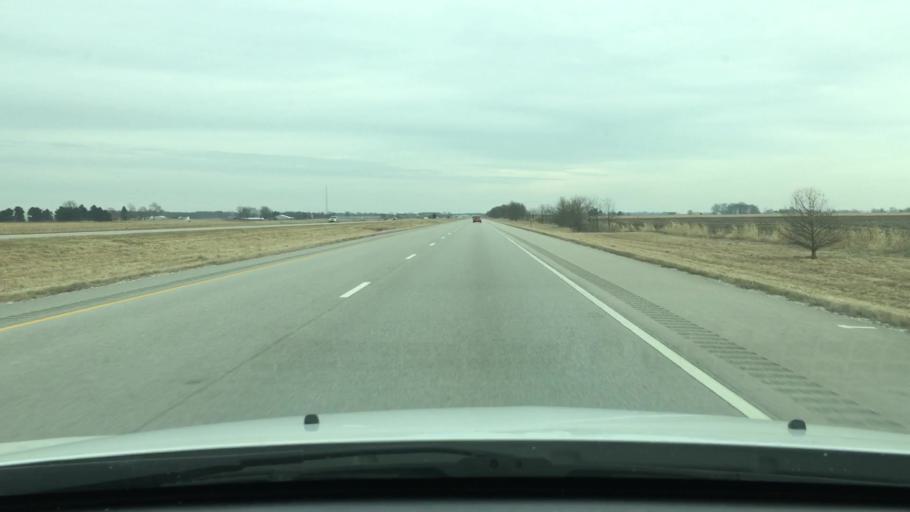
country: US
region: Illinois
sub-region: Sangamon County
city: New Berlin
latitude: 39.7366
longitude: -90.0101
